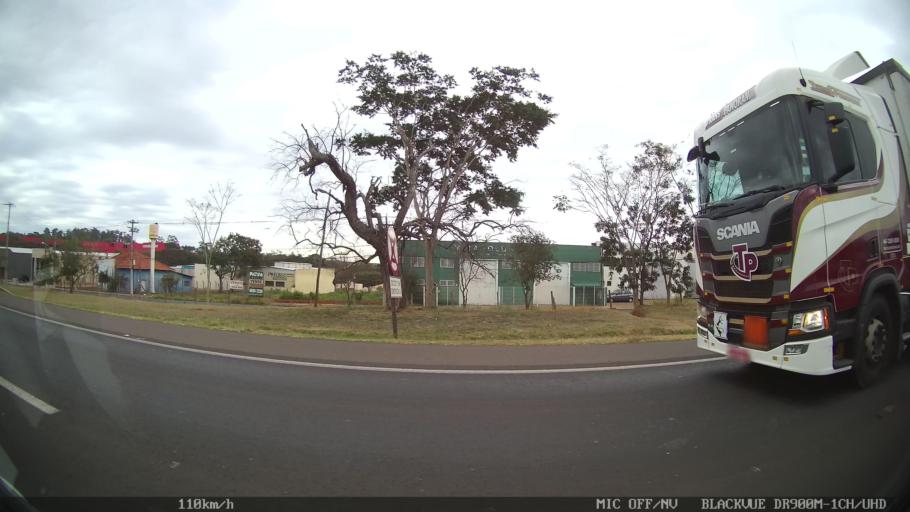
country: BR
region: Sao Paulo
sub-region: Bady Bassitt
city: Bady Bassitt
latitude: -20.8069
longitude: -49.5108
